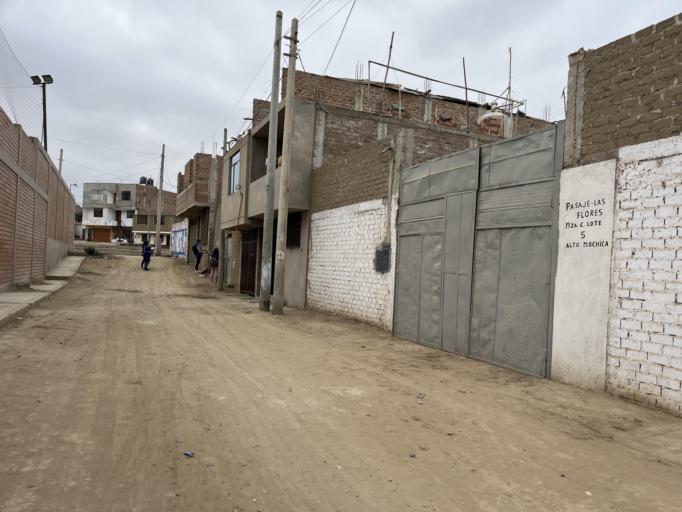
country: PE
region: La Libertad
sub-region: Provincia de Trujillo
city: La Esperanza
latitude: -8.0878
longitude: -79.0351
